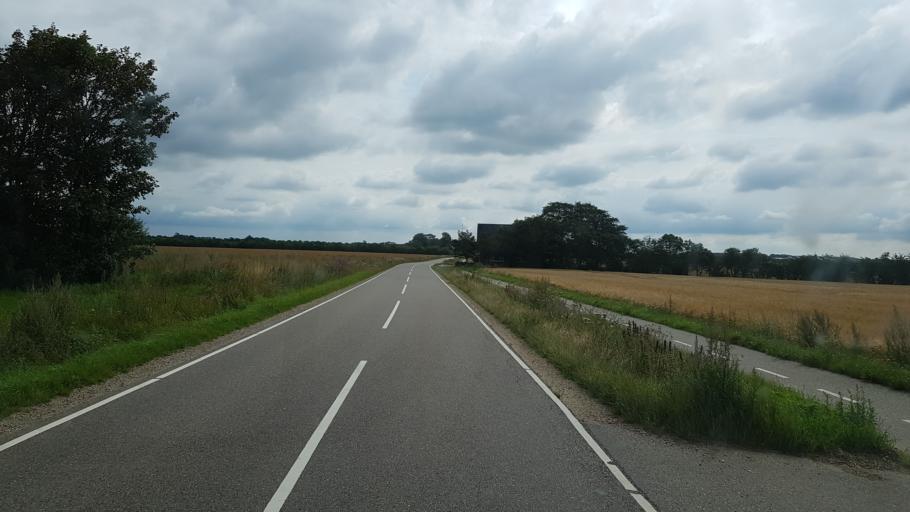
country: DK
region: South Denmark
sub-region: Varde Kommune
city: Varde
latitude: 55.7501
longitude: 8.4645
